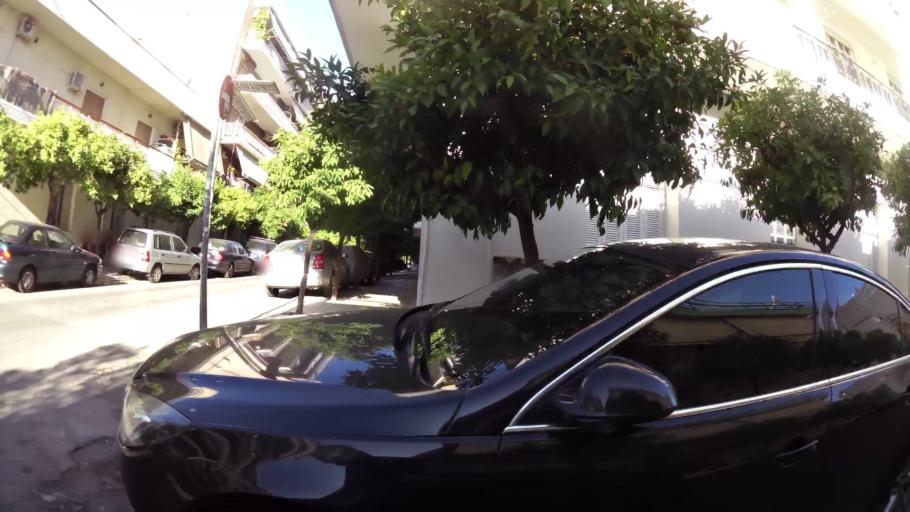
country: GR
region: Attica
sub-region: Nomos Piraios
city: Korydallos
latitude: 37.9779
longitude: 23.6568
